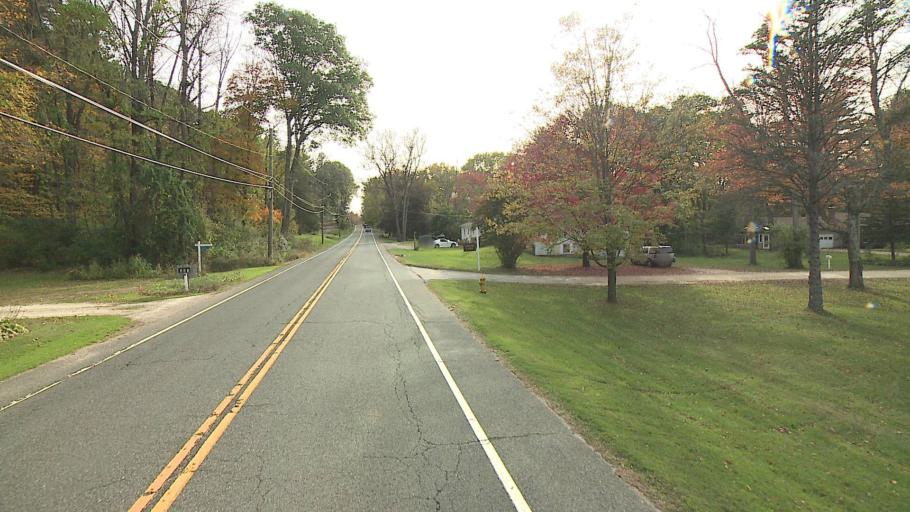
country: US
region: Connecticut
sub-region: Litchfield County
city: Canaan
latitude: 42.0121
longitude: -73.3534
